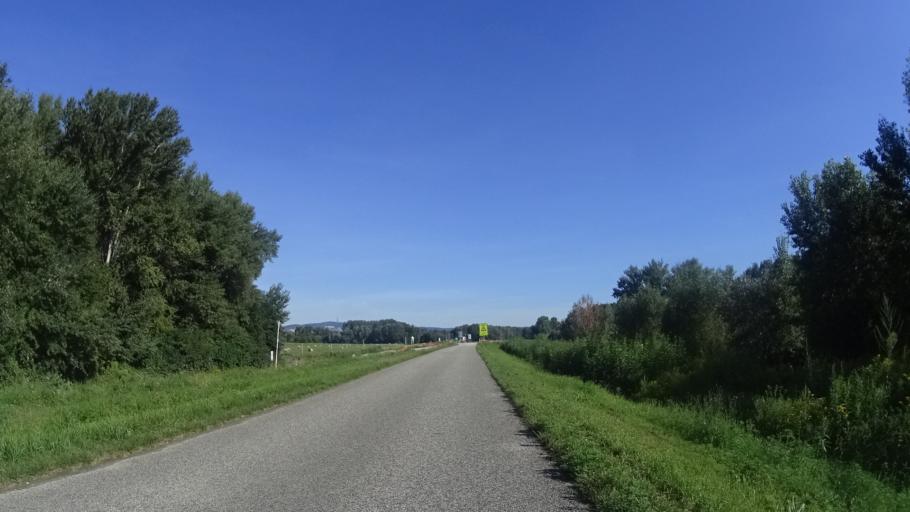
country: SK
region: Bratislavsky
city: Bratislava
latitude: 48.1043
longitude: 17.1471
